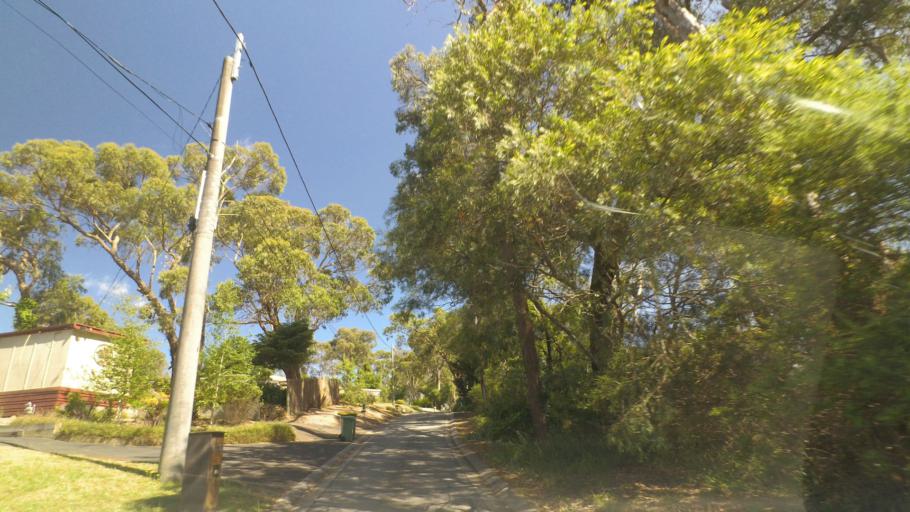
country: AU
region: Victoria
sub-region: Yarra Ranges
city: Kalorama
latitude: -37.8010
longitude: 145.3754
